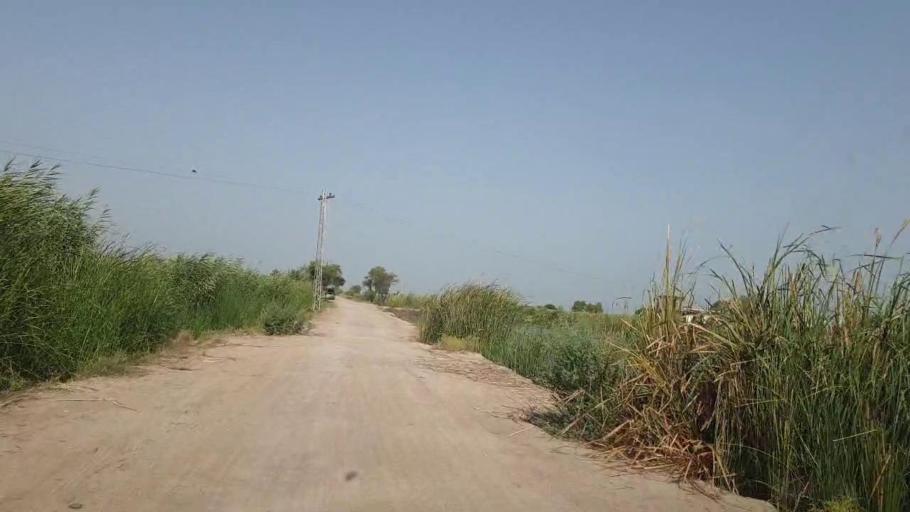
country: PK
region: Sindh
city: Sakrand
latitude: 26.3057
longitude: 68.2155
